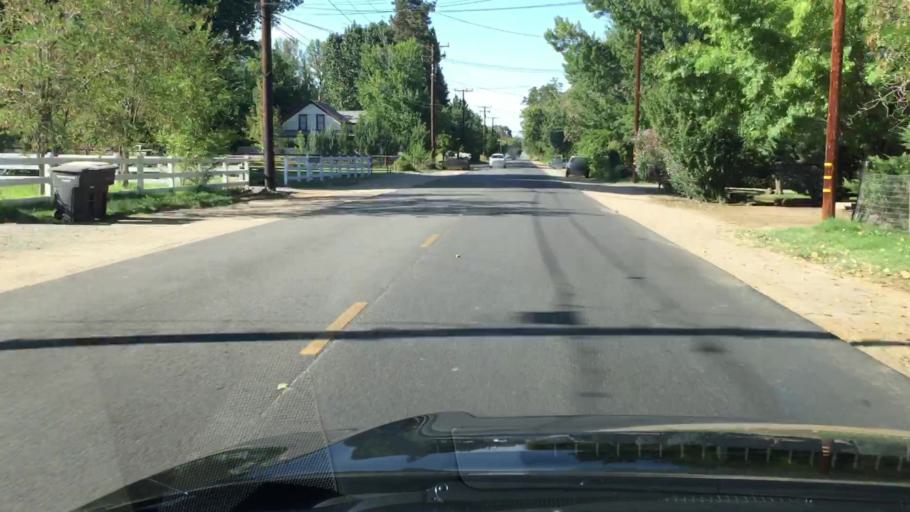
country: US
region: California
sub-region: Inyo County
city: Dixon Lane-Meadow Creek
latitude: 37.3713
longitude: -118.4321
